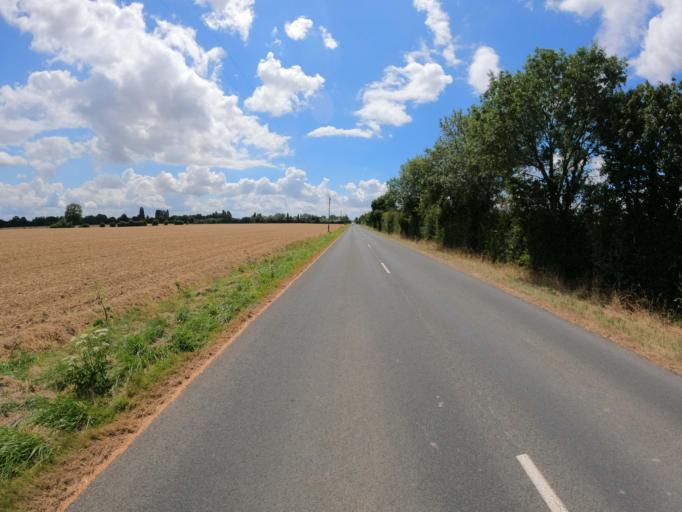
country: FR
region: Pays de la Loire
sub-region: Departement de Maine-et-Loire
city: Mire
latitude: 47.7388
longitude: -0.5094
